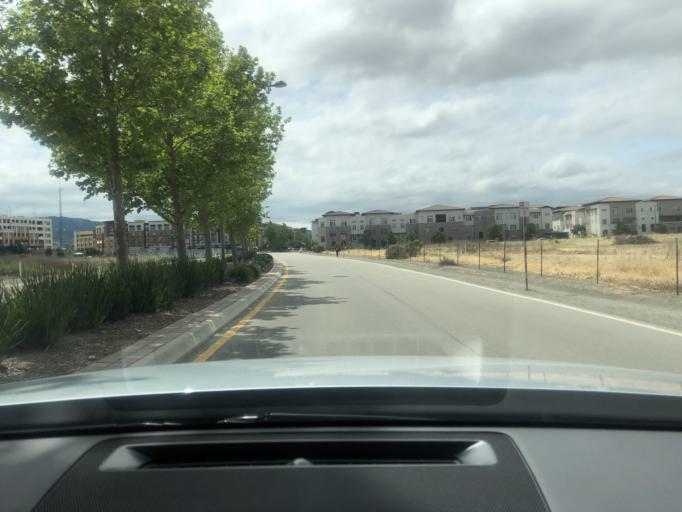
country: US
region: California
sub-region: Alameda County
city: Dublin
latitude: 37.7047
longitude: -121.8940
